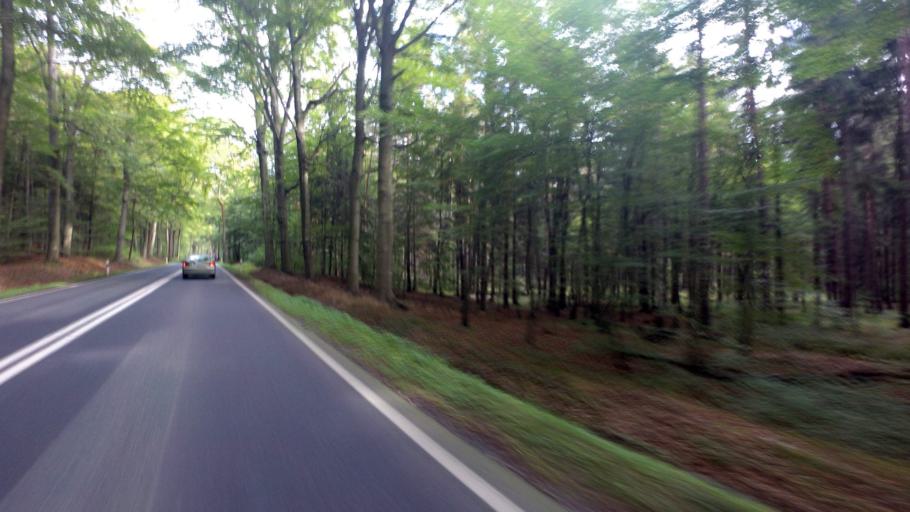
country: DE
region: Saxony
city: Ottendorf-Okrilla
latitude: 51.2183
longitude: 13.8419
